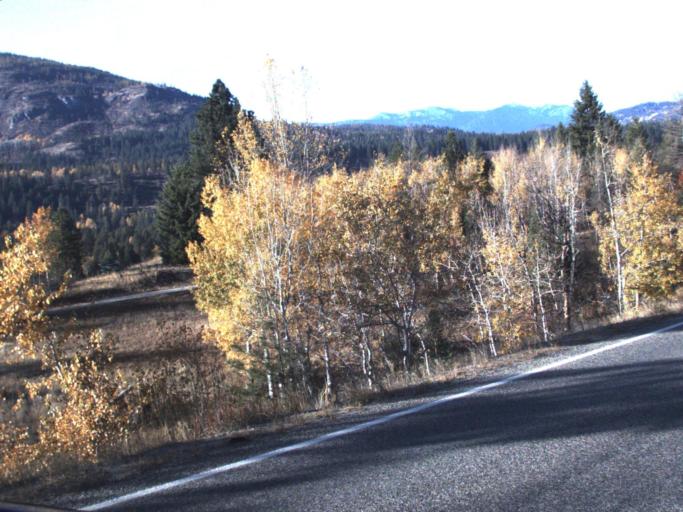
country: CA
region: British Columbia
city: Rossland
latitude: 48.9055
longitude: -117.7931
